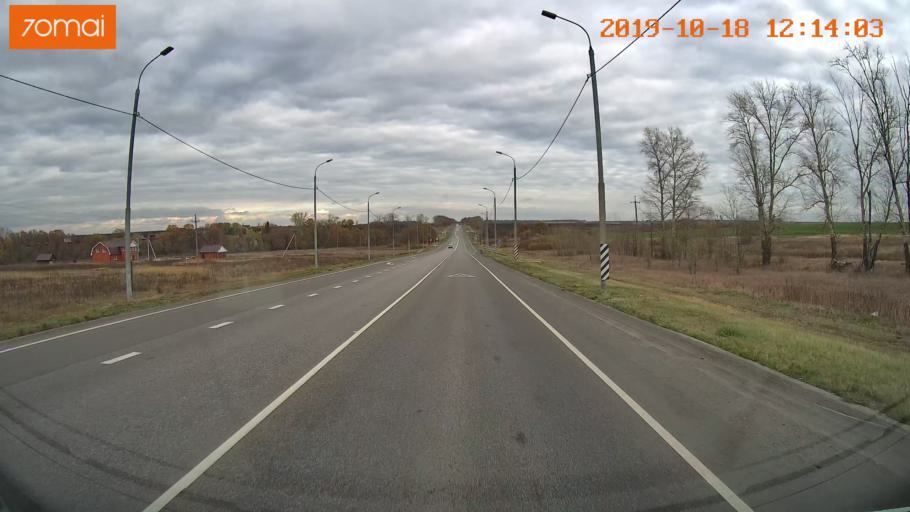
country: RU
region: Rjazan
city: Zakharovo
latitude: 54.4258
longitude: 39.3767
